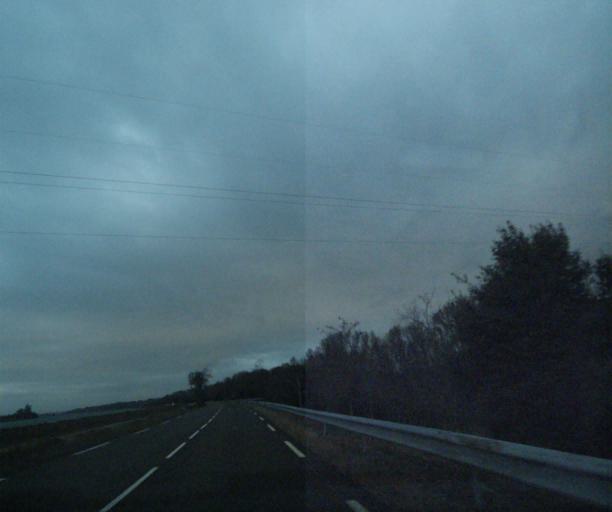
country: FR
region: Rhone-Alpes
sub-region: Departement de l'Ardeche
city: Cornas
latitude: 44.9777
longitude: 4.8561
